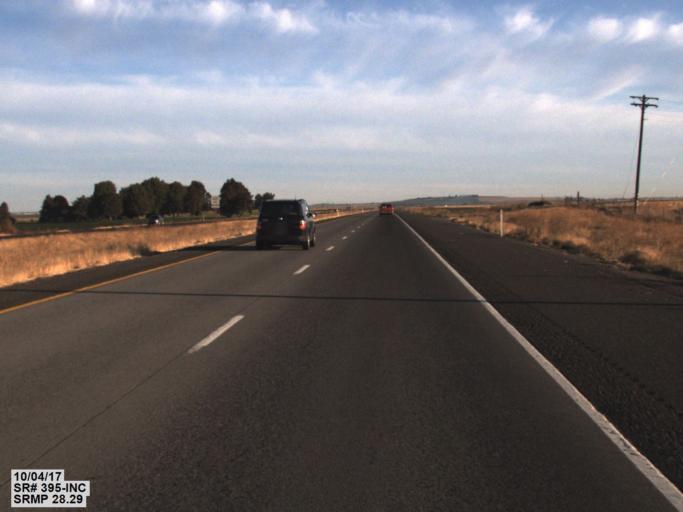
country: US
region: Washington
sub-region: Franklin County
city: Pasco
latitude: 46.3312
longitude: -119.0927
